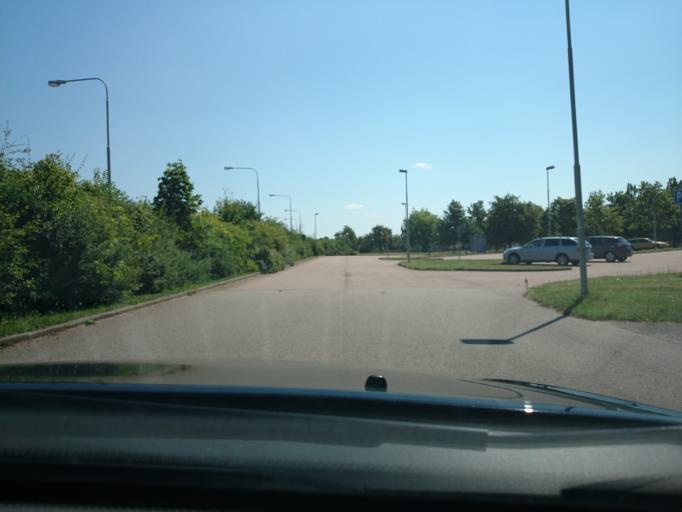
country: SE
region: Skane
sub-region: Landskrona
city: Landskrona
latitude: 55.8888
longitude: 12.8183
